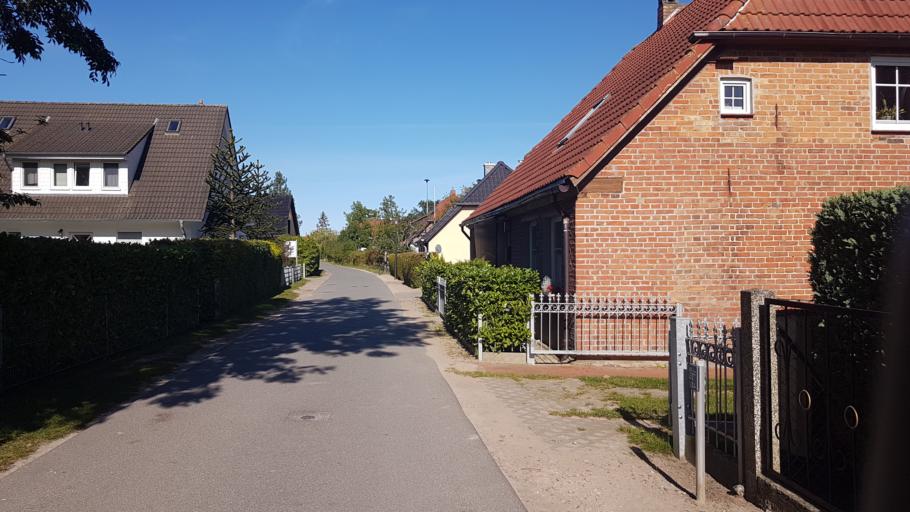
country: DE
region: Mecklenburg-Vorpommern
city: Glowe
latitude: 54.5680
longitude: 13.4735
